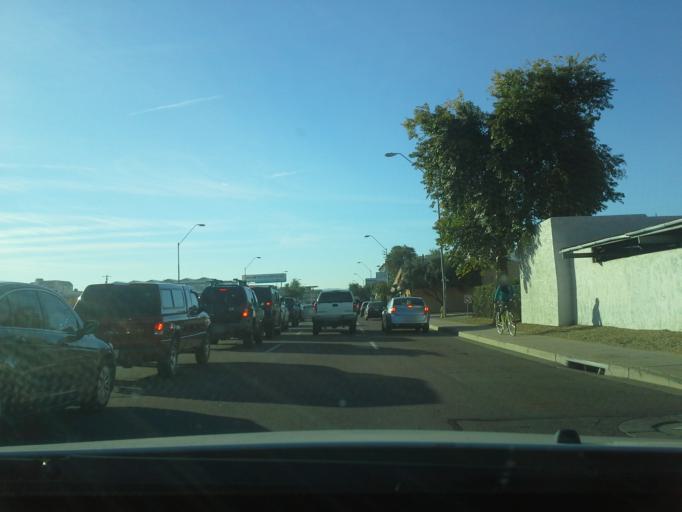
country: US
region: Arizona
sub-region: Maricopa County
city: Phoenix
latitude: 33.4548
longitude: -112.0827
